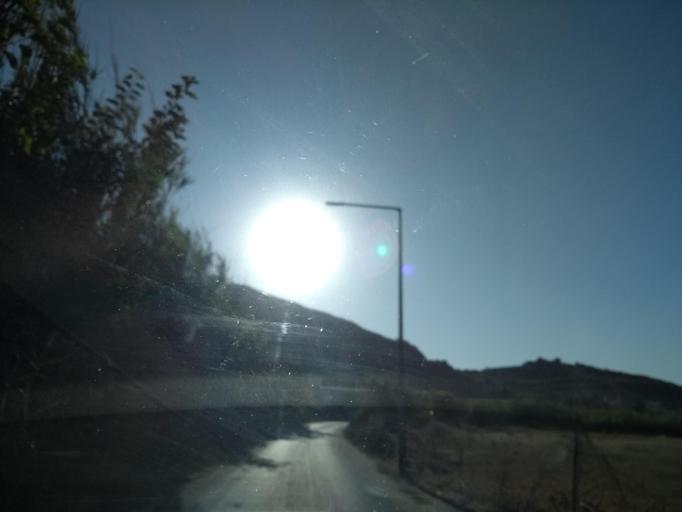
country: GR
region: Crete
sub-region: Nomos Chanias
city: Kalivai
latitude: 35.4642
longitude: 24.1573
